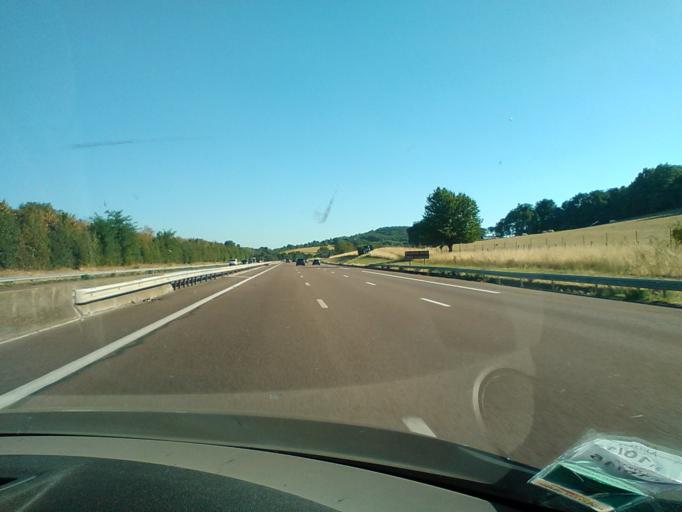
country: DE
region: Bavaria
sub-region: Upper Bavaria
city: Gaimersheim
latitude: 48.7849
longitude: 11.3923
